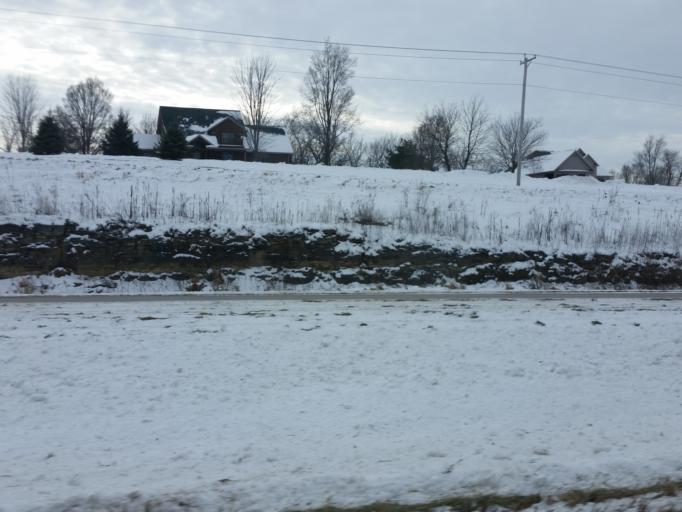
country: US
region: Iowa
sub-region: Dubuque County
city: Dyersville
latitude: 42.4696
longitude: -91.0879
